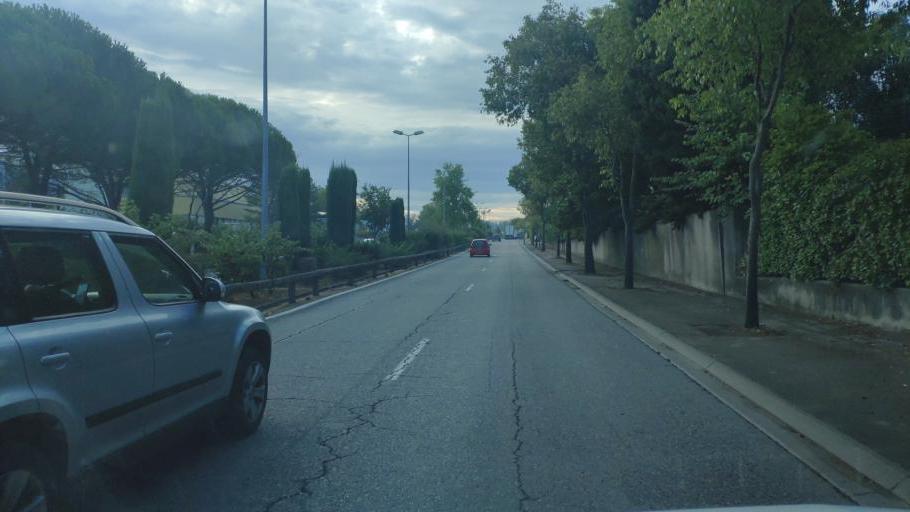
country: FR
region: Provence-Alpes-Cote d'Azur
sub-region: Departement des Bouches-du-Rhone
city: Cabries
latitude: 43.4862
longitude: 5.3798
